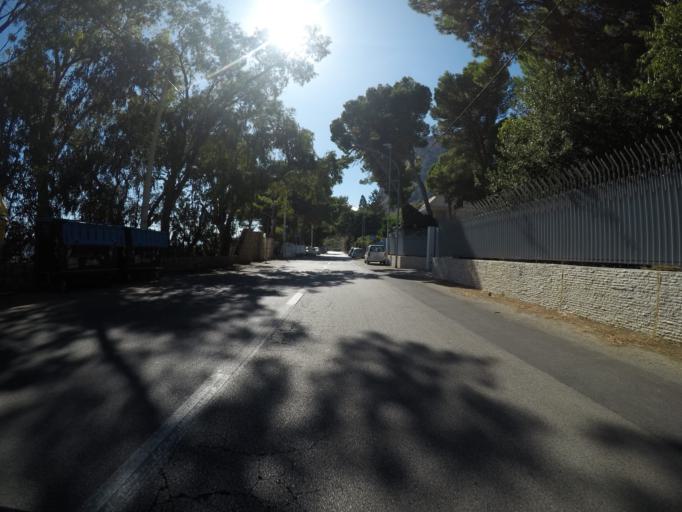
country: IT
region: Sicily
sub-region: Palermo
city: Palermo
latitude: 38.1885
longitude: 13.3597
